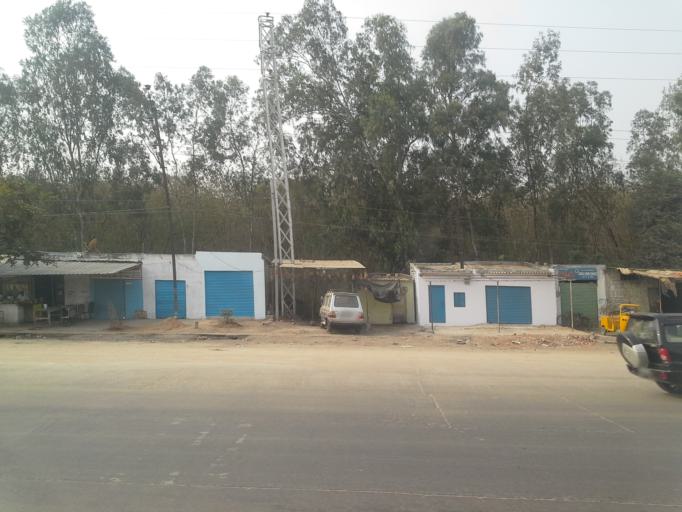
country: IN
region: Telangana
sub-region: Medak
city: Patancheru
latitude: 17.5229
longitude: 78.2741
